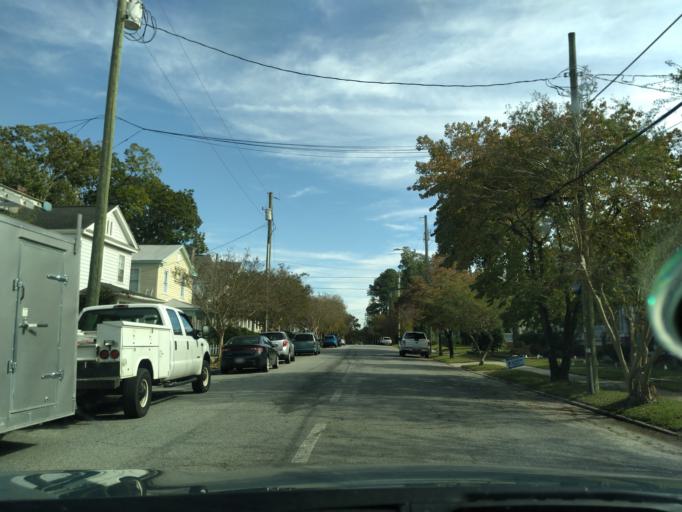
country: US
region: North Carolina
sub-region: Beaufort County
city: Washington
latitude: 35.5383
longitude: -77.0467
